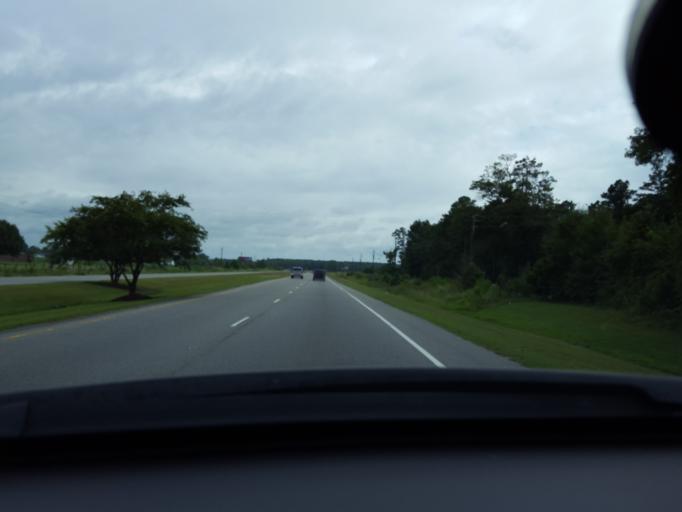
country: US
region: North Carolina
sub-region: Pitt County
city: Ayden
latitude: 35.4729
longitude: -77.4357
